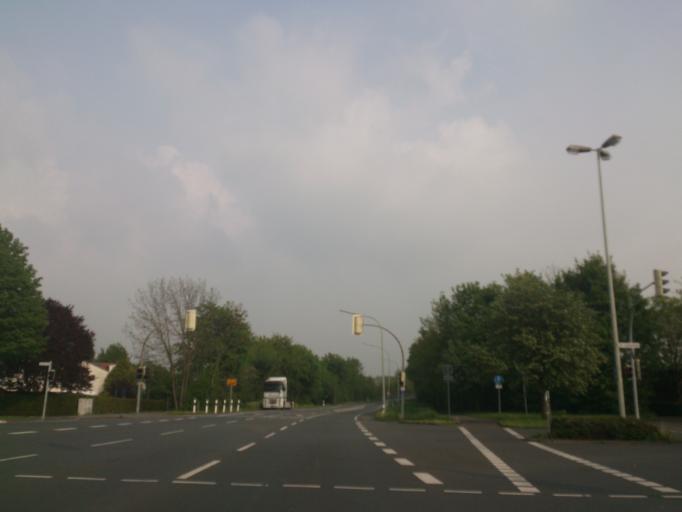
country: DE
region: North Rhine-Westphalia
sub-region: Regierungsbezirk Detmold
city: Paderborn
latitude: 51.7077
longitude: 8.7857
